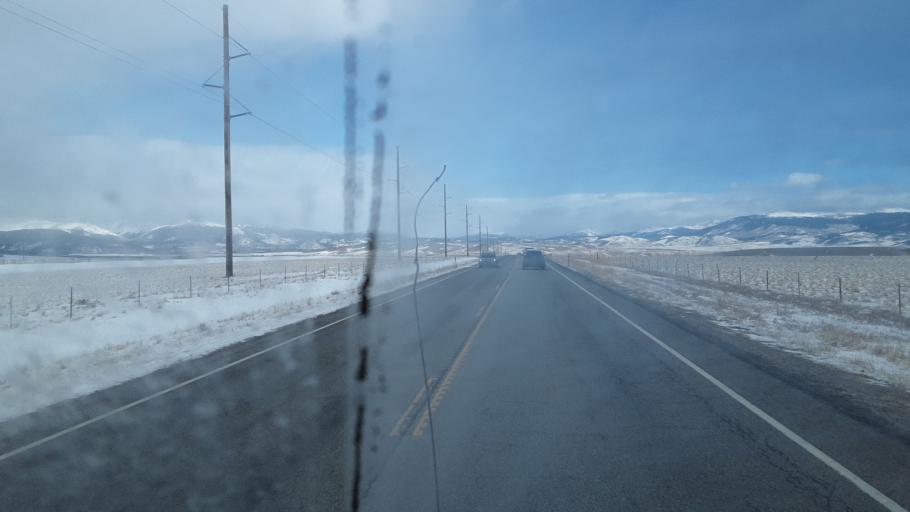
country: US
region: Colorado
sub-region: Park County
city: Fairplay
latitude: 39.3252
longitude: -105.8736
